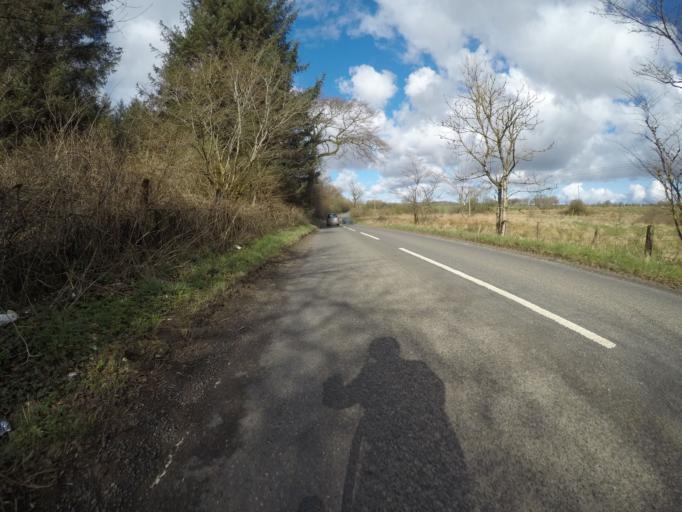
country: GB
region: Scotland
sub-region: North Ayrshire
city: Beith
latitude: 55.7334
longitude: -4.6138
